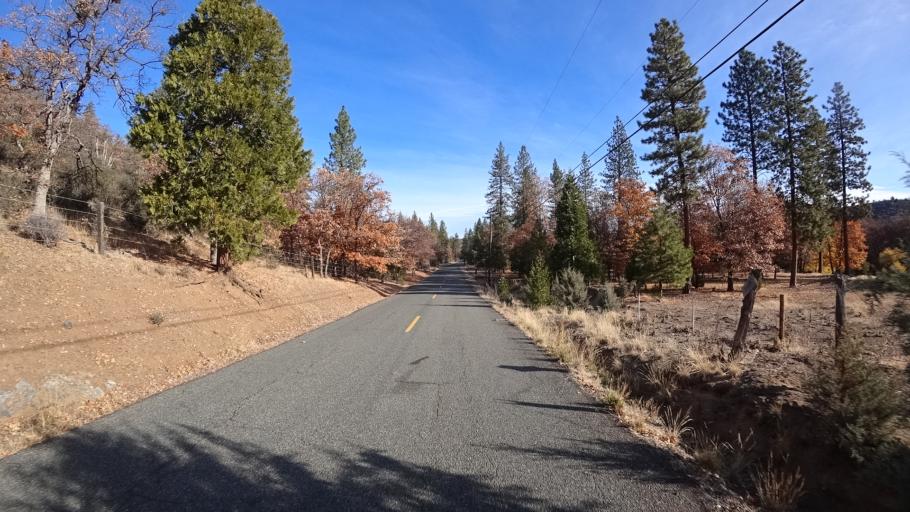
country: US
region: California
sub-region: Siskiyou County
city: Yreka
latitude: 41.6541
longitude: -122.6287
